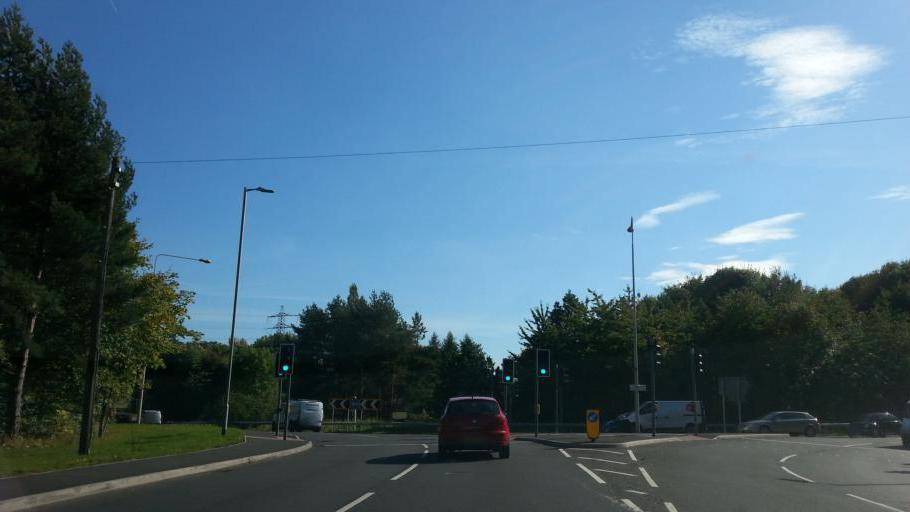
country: GB
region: England
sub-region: Shropshire
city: Hadley
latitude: 52.6970
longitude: -2.4927
